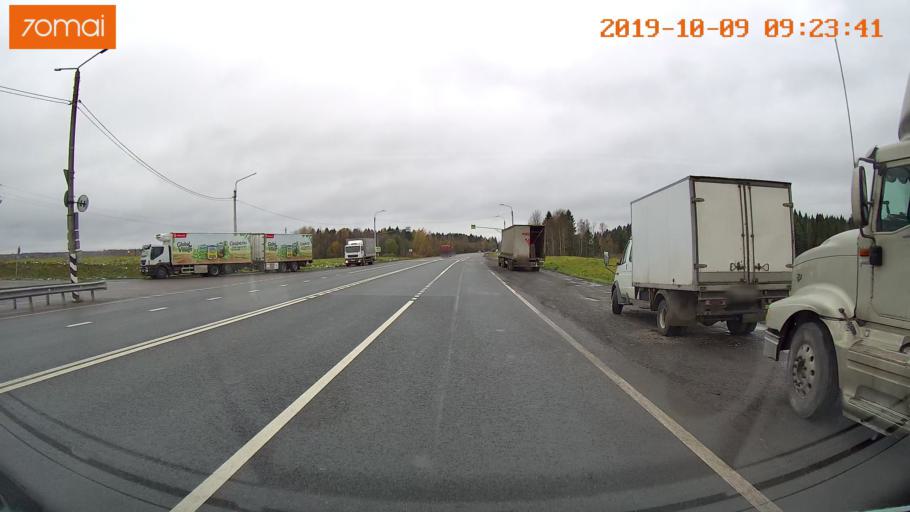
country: RU
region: Vologda
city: Vologda
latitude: 59.0728
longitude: 40.0268
